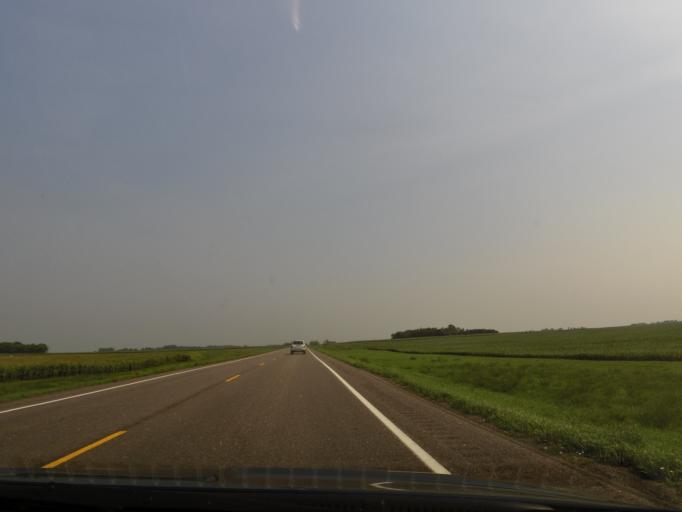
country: US
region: South Dakota
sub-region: Roberts County
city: Sisseton
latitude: 45.8488
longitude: -97.0545
